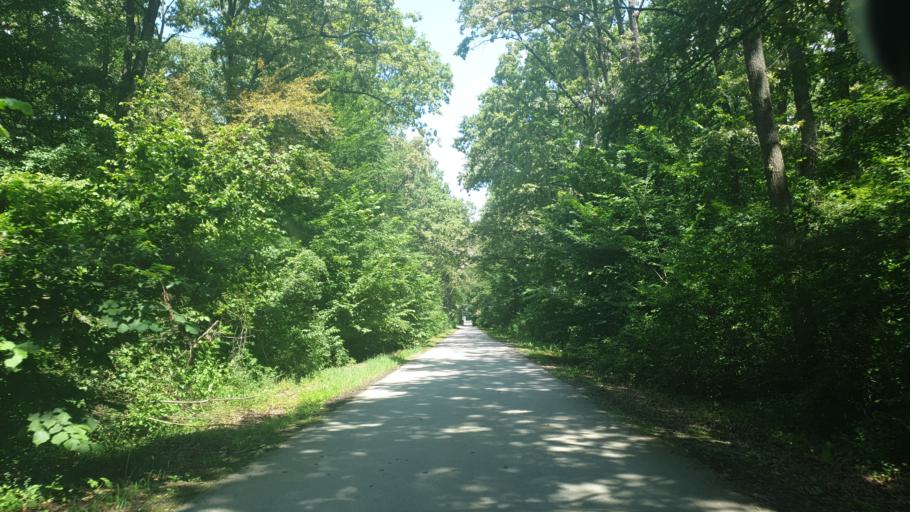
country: RS
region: Autonomna Pokrajina Vojvodina
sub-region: Sremski Okrug
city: Sid
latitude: 45.0404
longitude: 19.1383
